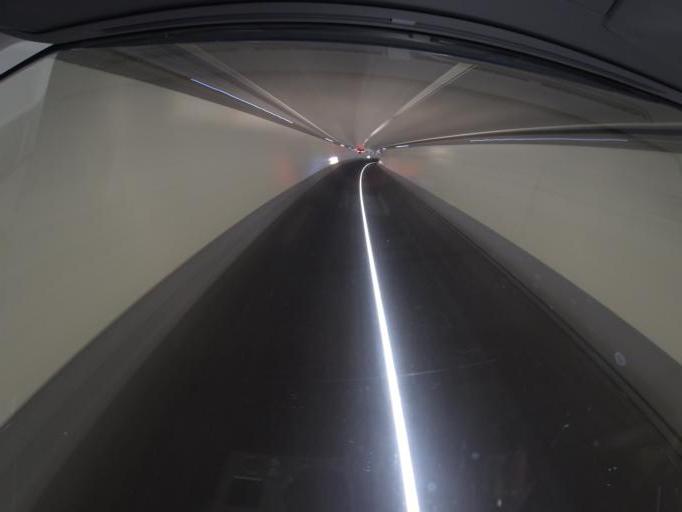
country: CH
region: Saint Gallen
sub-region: Wahlkreis Sarganserland
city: Quarten
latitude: 47.1096
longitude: 9.2415
